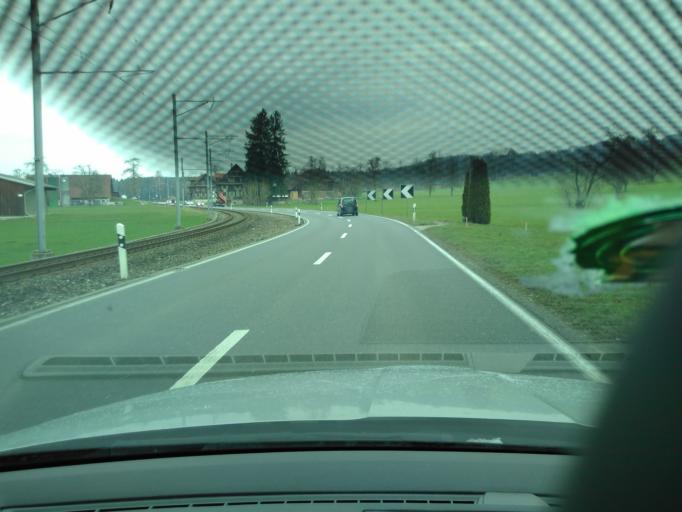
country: CH
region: Lucerne
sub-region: Hochdorf District
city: Hochdorf
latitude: 47.1929
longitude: 8.2800
